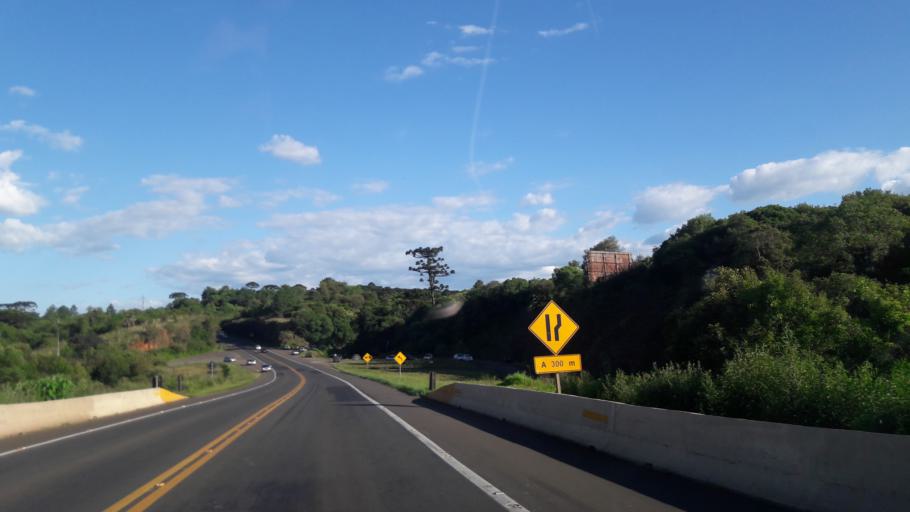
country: BR
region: Parana
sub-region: Guarapuava
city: Guarapuava
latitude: -25.3568
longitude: -51.3600
